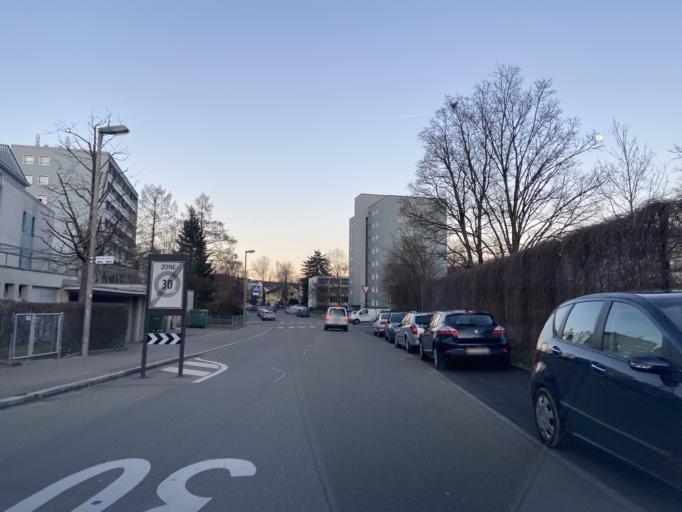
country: CH
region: Zurich
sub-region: Bezirk Winterthur
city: Wuelflingen (Kreis 6) / Haerti
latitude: 47.5124
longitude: 8.6837
